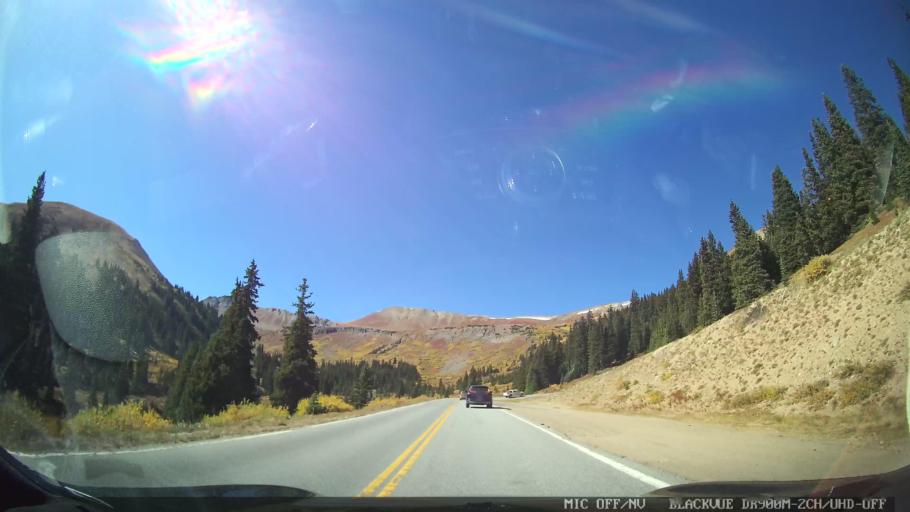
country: US
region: Colorado
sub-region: Pitkin County
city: Aspen
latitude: 39.0996
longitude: -106.5690
